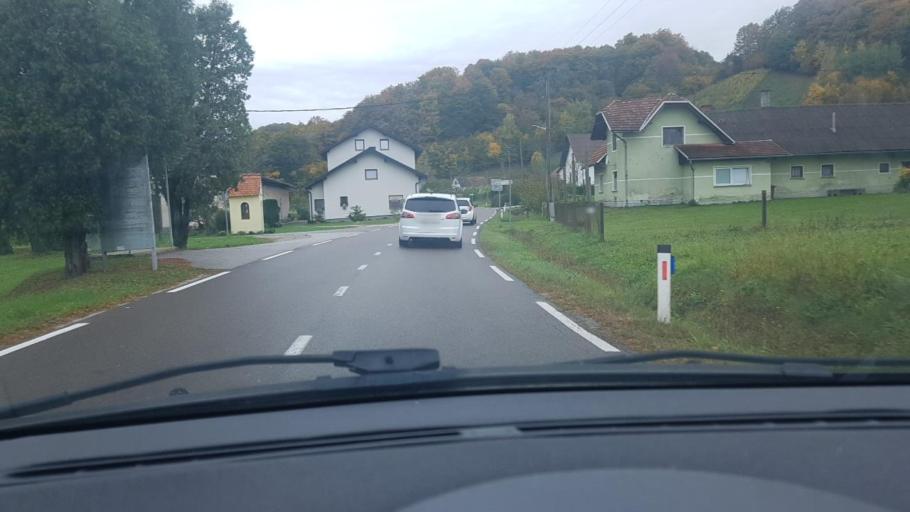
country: SI
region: Majsperk
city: Majsperk
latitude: 46.3298
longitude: 15.7257
